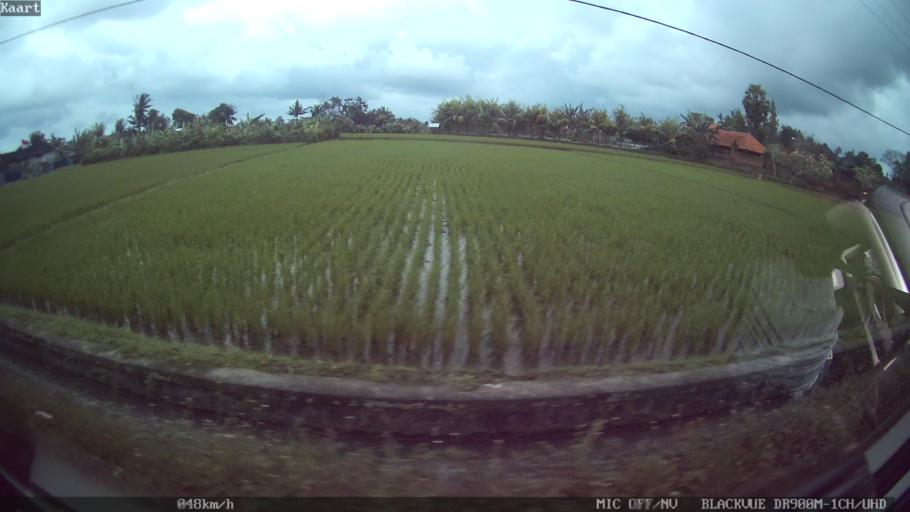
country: ID
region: Bali
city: Banjar Cemenggon
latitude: -8.5568
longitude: 115.1901
